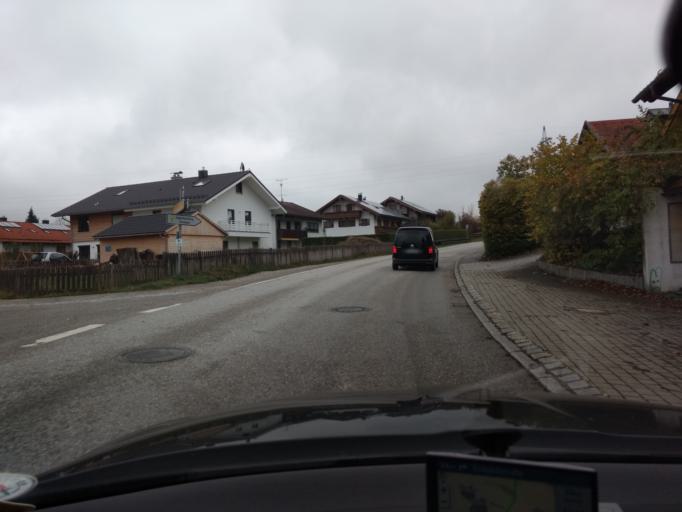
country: DE
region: Bavaria
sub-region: Upper Bavaria
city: Konigsdorf
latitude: 47.8162
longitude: 11.4819
